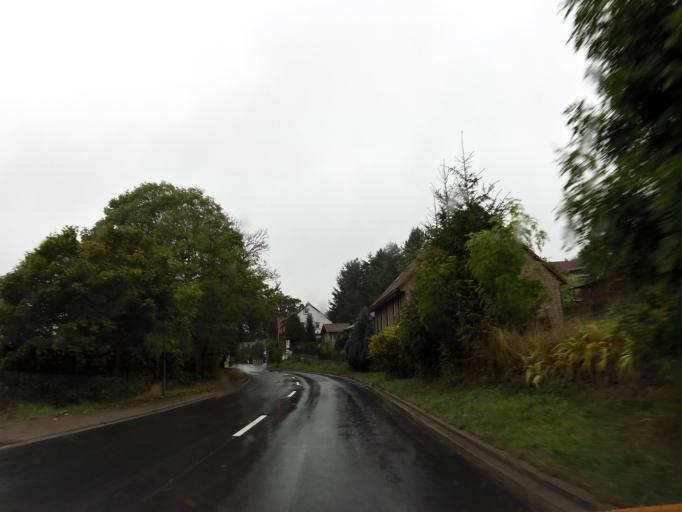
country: DE
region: Saxony-Anhalt
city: Hasselfelde
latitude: 51.6655
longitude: 10.8942
